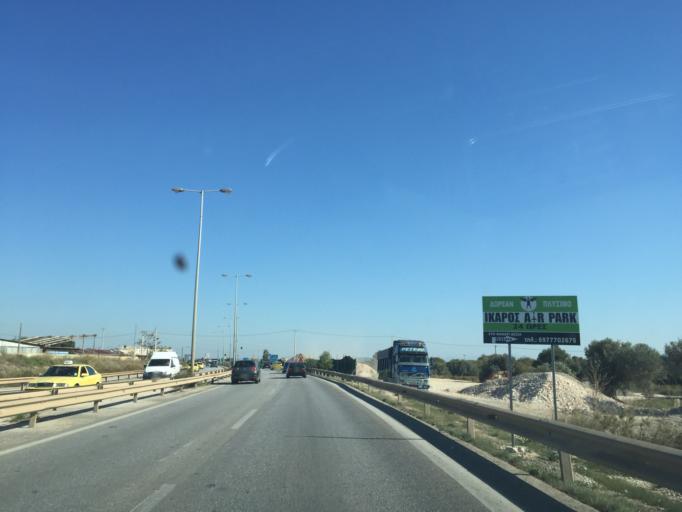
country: GR
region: Attica
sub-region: Nomarchia Anatolikis Attikis
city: Koropi
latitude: 37.9009
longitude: 23.8920
